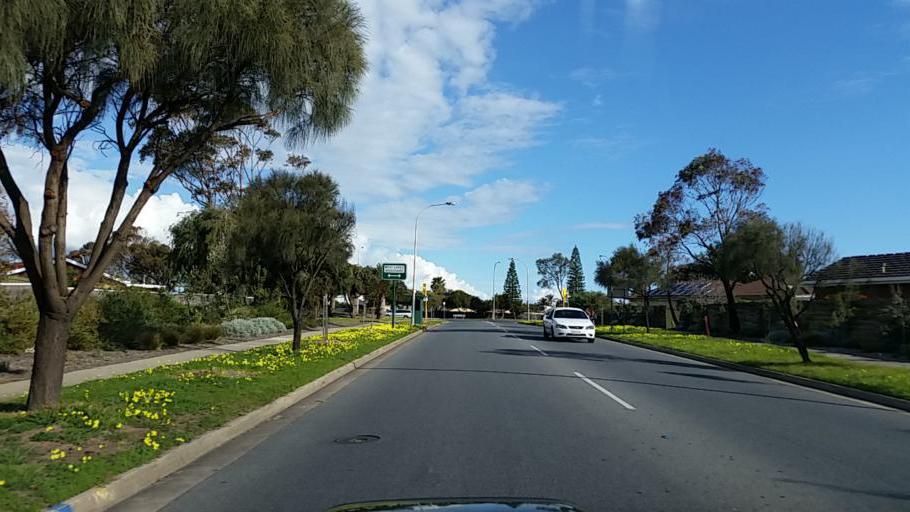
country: AU
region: South Australia
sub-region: Charles Sturt
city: West Lakes Shore
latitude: -34.8702
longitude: 138.4837
